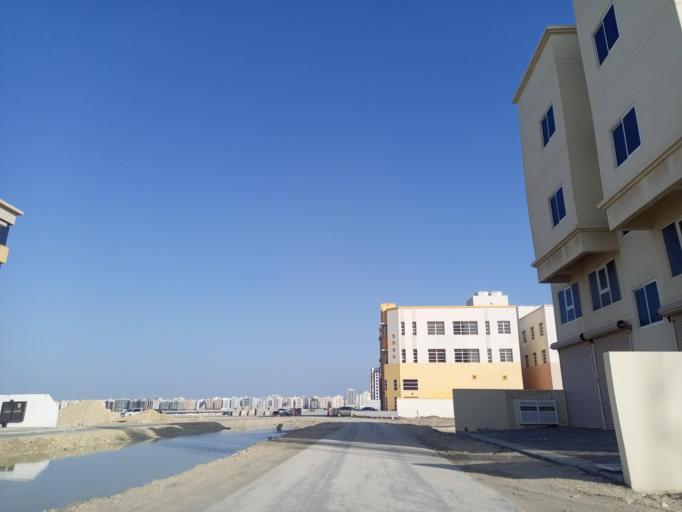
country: BH
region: Muharraq
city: Al Hadd
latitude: 26.2265
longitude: 50.6321
